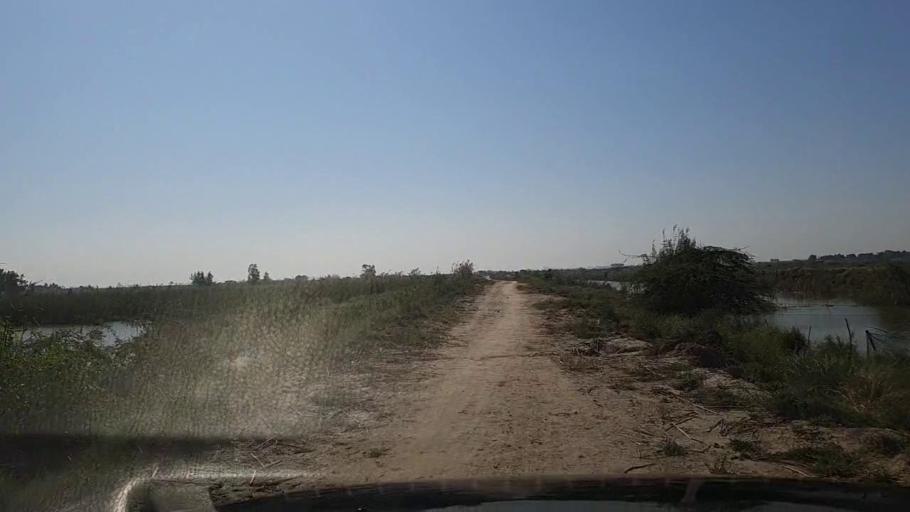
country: PK
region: Sindh
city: Thatta
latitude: 24.6727
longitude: 67.8889
